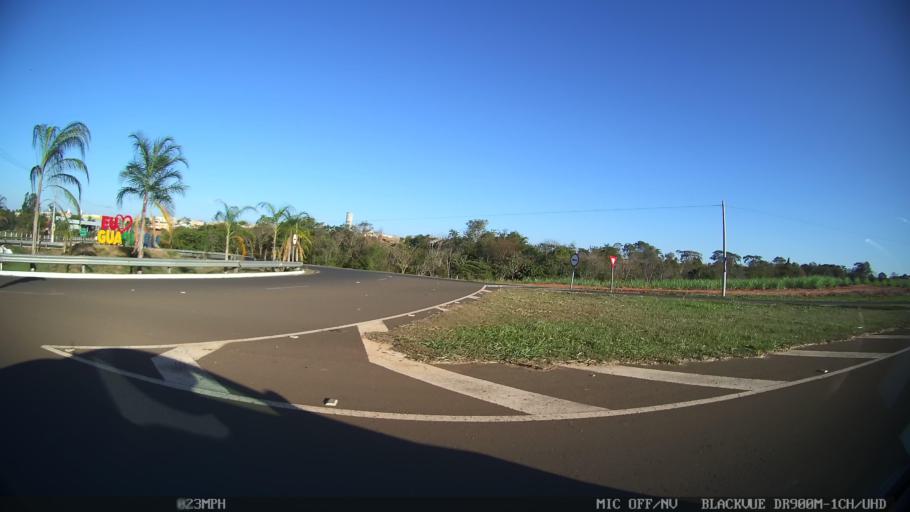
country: BR
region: Sao Paulo
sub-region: Guapiacu
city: Guapiacu
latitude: -20.7873
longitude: -49.2405
